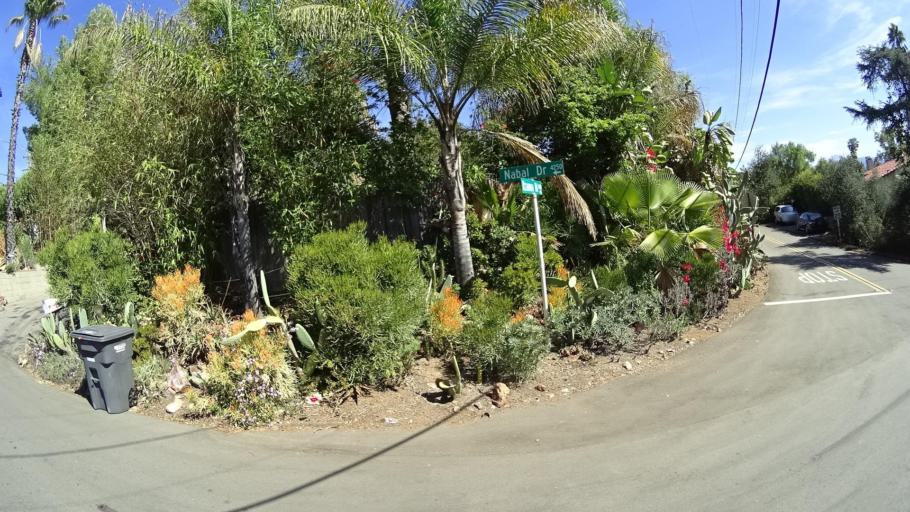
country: US
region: California
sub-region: San Diego County
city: Casa de Oro-Mount Helix
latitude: 32.7568
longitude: -116.9658
